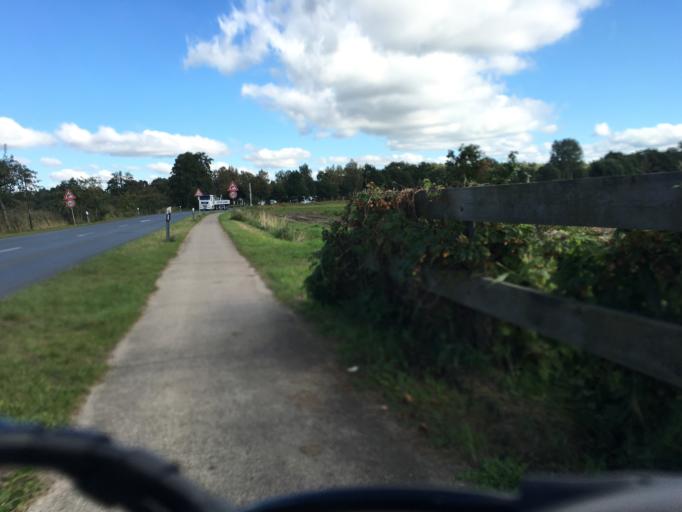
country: DE
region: Lower Saxony
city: Bardowick
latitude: 53.3025
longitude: 10.4003
